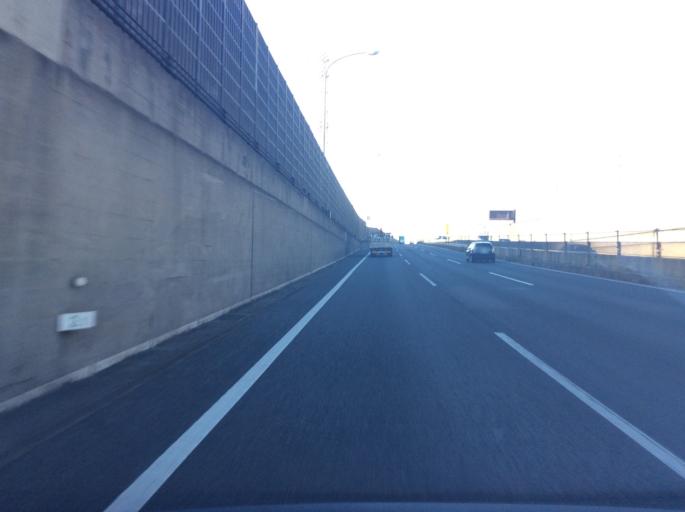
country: JP
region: Chiba
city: Nagareyama
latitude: 35.8498
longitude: 139.8753
